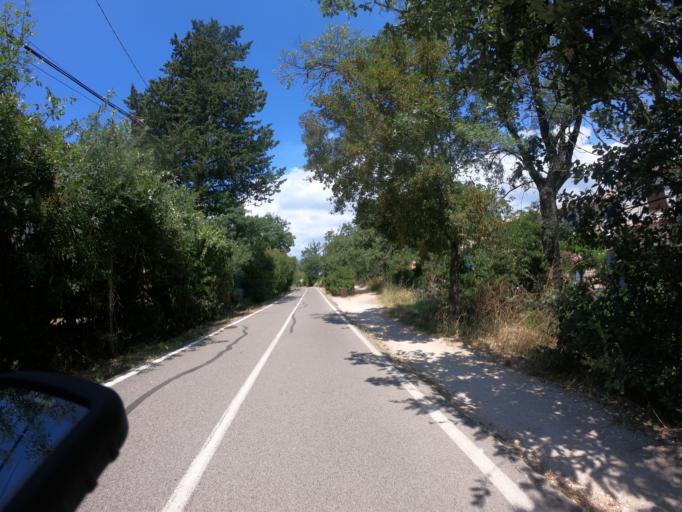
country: FR
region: Provence-Alpes-Cote d'Azur
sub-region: Departement du Var
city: La Valette-du-Var
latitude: 43.1164
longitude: 5.9757
